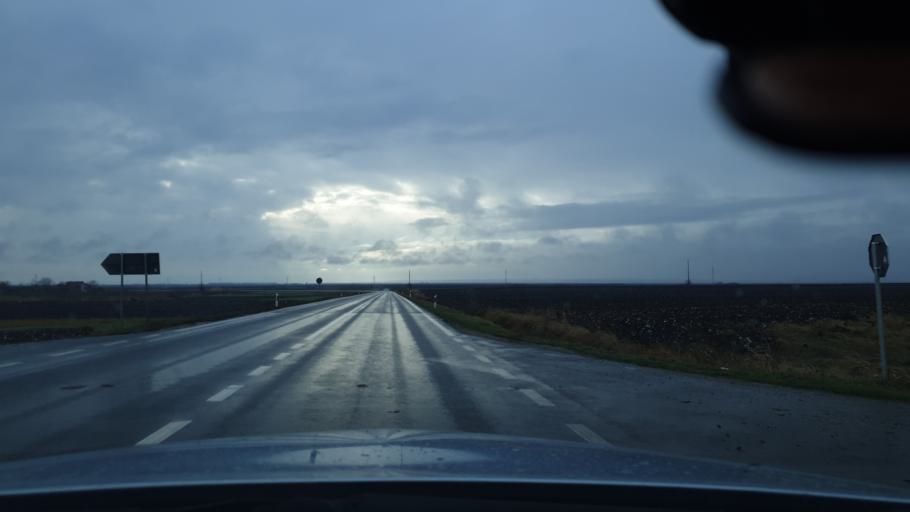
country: RS
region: Autonomna Pokrajina Vojvodina
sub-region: Juznobanatski Okrug
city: Kovin
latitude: 44.8153
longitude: 20.8554
